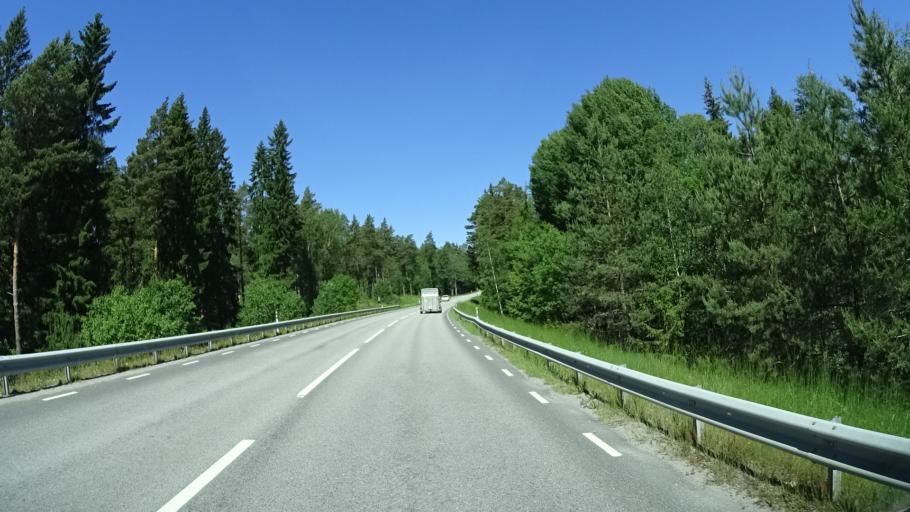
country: SE
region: Stockholm
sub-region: Vallentuna Kommun
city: Vallentuna
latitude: 59.5696
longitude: 18.0986
